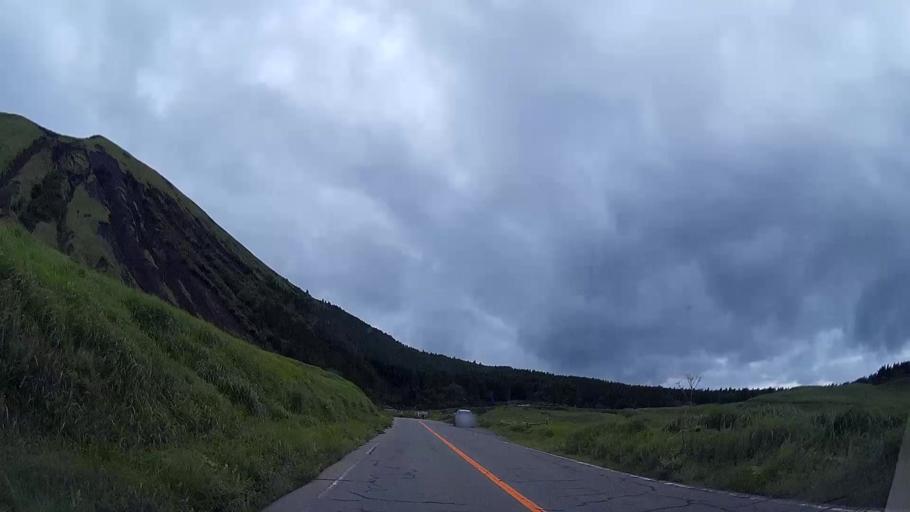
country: JP
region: Kumamoto
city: Aso
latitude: 32.9002
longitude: 131.0518
